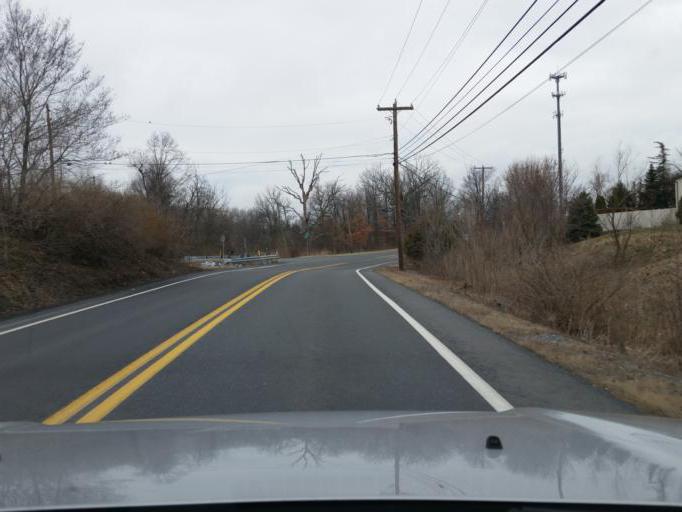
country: US
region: Pennsylvania
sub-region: Dauphin County
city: Paxtonia
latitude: 40.3159
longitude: -76.7781
